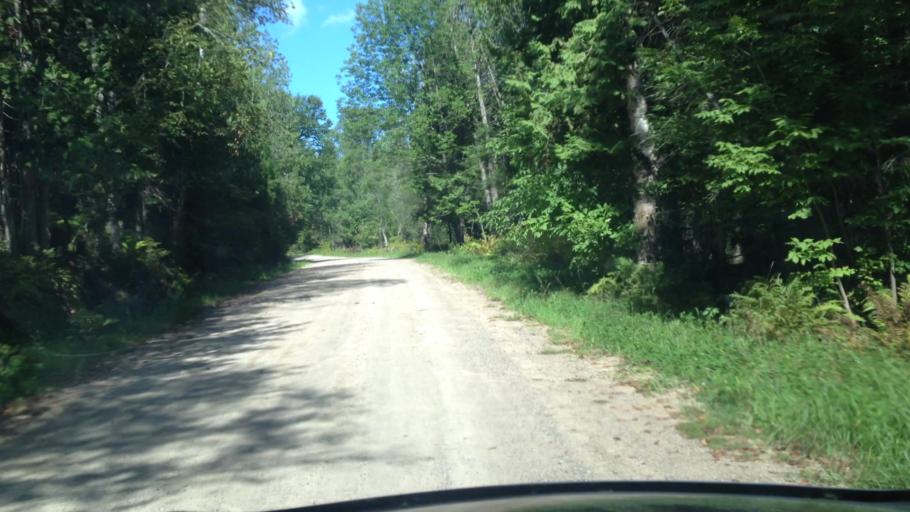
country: CA
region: Quebec
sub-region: Laurentides
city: Brownsburg-Chatham
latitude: 45.9190
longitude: -74.5770
